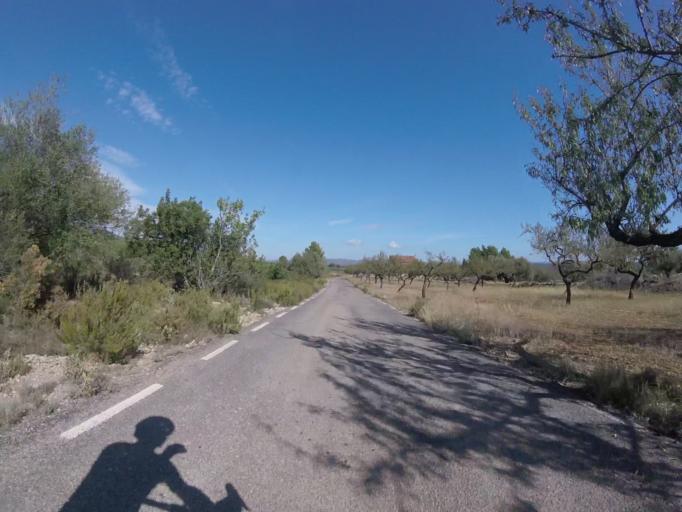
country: ES
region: Valencia
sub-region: Provincia de Castello
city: Sarratella
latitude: 40.2798
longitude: 0.0660
